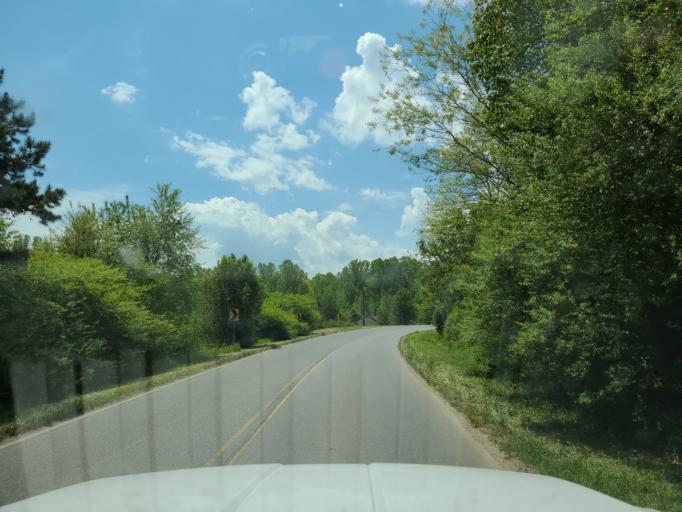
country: US
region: North Carolina
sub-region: Cleveland County
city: Shelby
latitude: 35.3232
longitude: -81.4901
